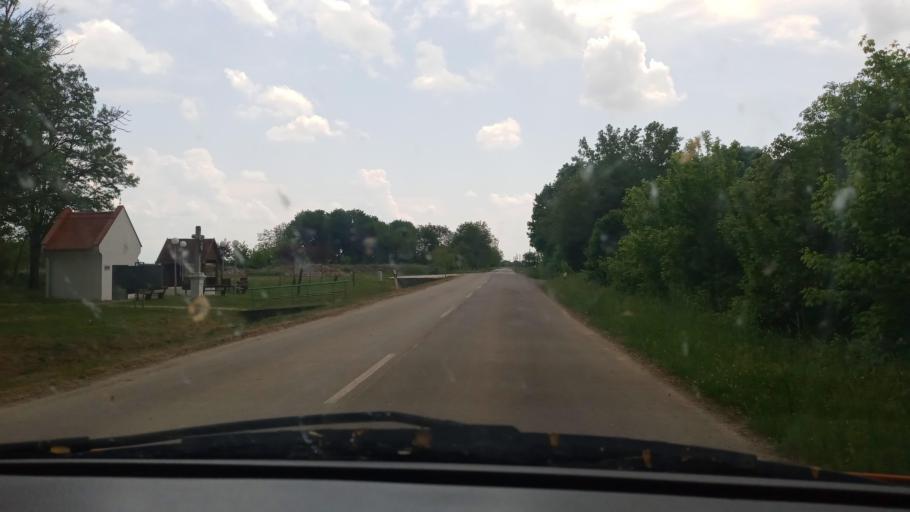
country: HU
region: Baranya
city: Beremend
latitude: 45.7752
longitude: 18.4439
